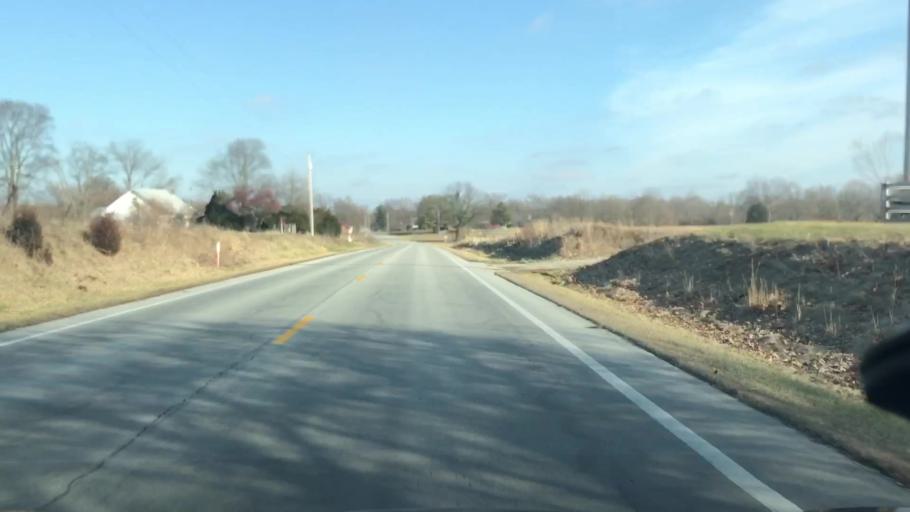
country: US
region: Ohio
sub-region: Greene County
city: Yellow Springs
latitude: 39.7972
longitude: -83.9288
